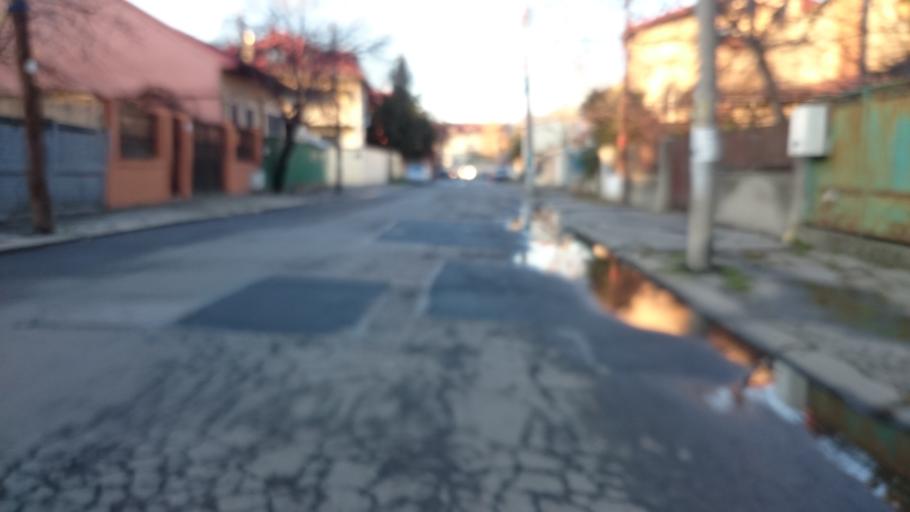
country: RO
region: Bucuresti
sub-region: Municipiul Bucuresti
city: Bucuresti
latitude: 44.4199
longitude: 26.0580
